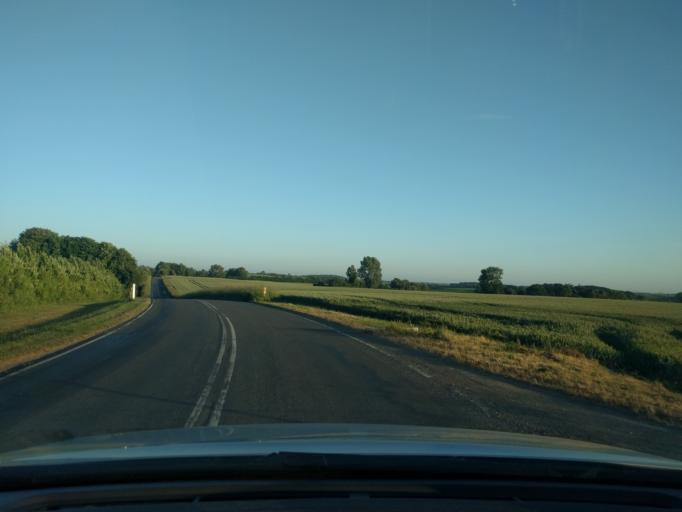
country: DK
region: South Denmark
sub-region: Kerteminde Kommune
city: Kerteminde
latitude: 55.5664
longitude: 10.6460
